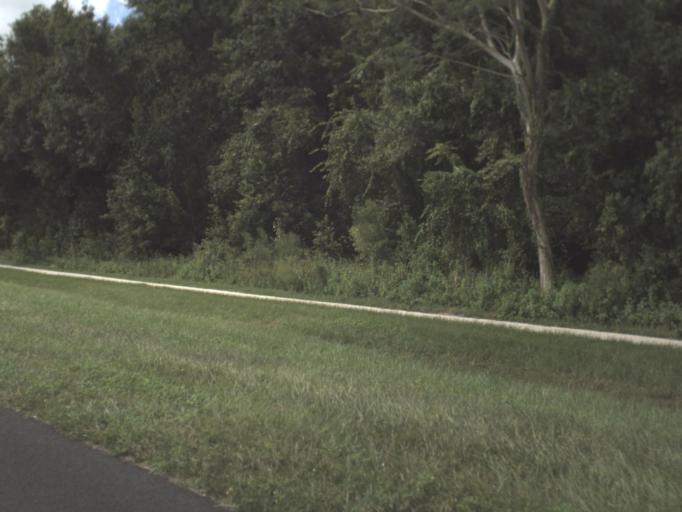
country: US
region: Florida
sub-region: Hardee County
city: Wauchula
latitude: 27.5849
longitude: -81.8199
